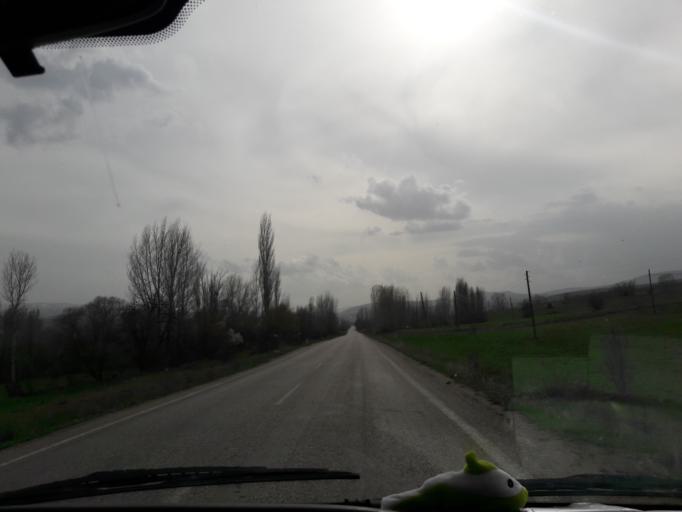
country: TR
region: Gumushane
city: Siran
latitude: 40.1682
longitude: 39.0620
